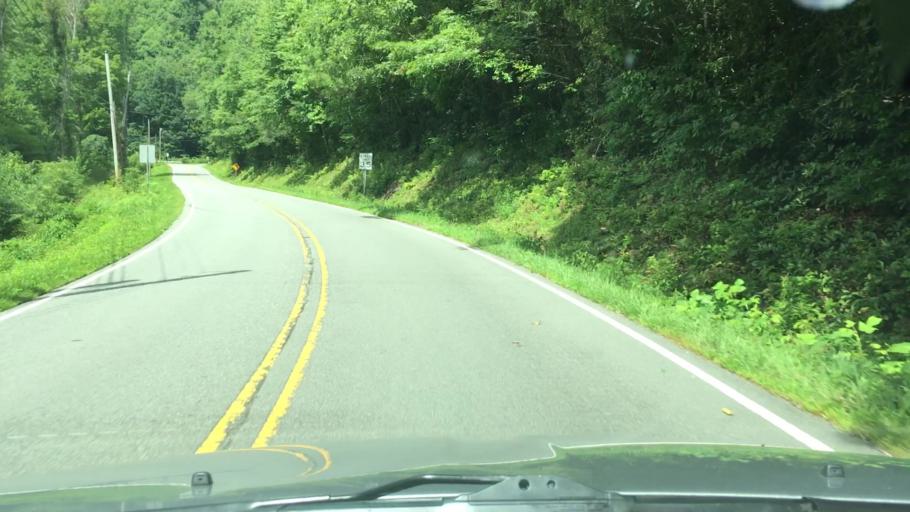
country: US
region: North Carolina
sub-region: Yancey County
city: Burnsville
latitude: 35.7930
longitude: -82.2017
